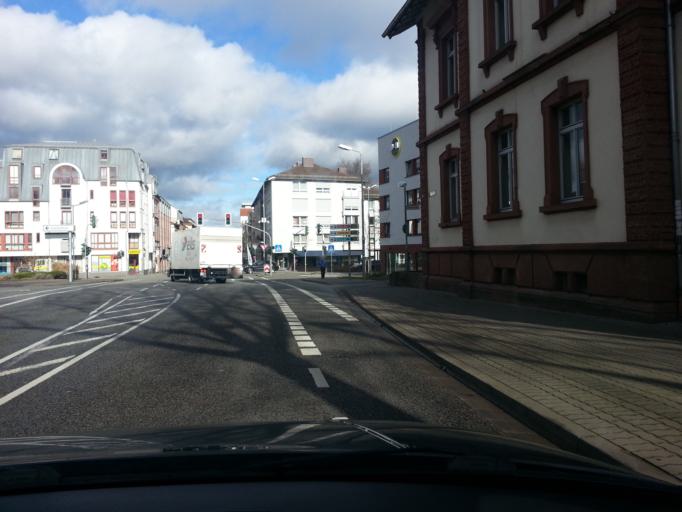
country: DE
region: Rheinland-Pfalz
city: Kaiserslautern
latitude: 49.4372
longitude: 7.7724
